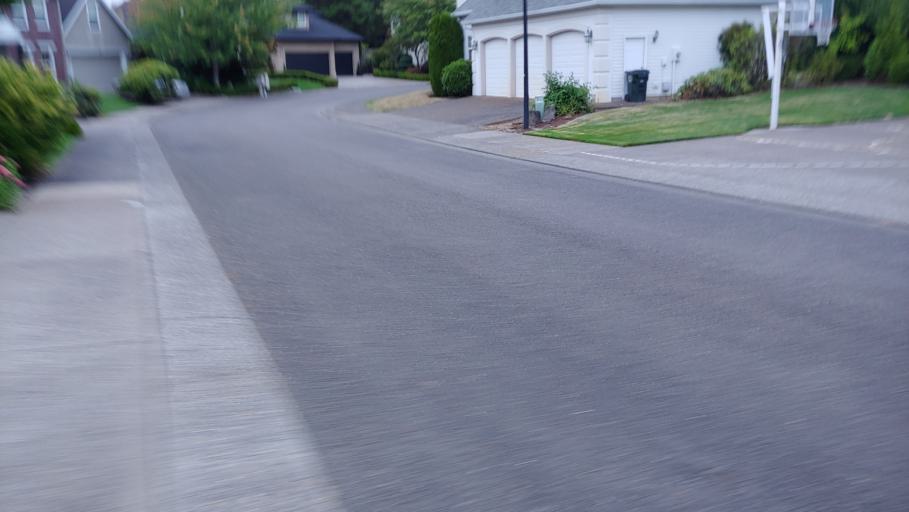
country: US
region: Oregon
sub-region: Washington County
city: Cedar Mill
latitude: 45.5357
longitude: -122.8224
